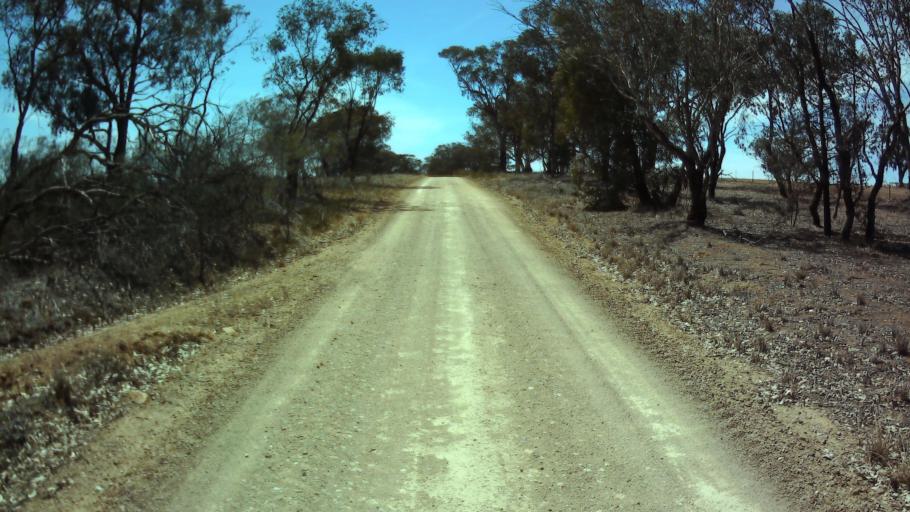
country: AU
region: New South Wales
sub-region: Weddin
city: Grenfell
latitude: -33.9426
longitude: 148.1418
